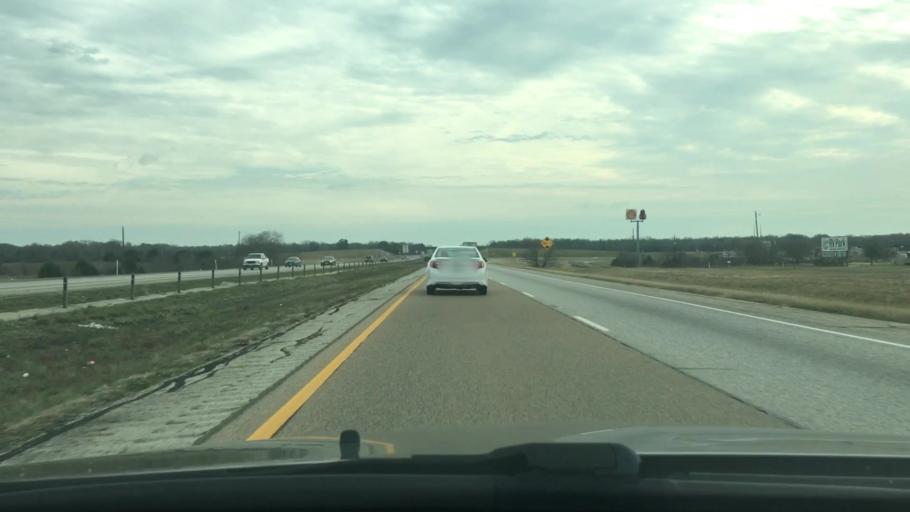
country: US
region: Texas
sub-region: Madison County
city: Madisonville
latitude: 31.0976
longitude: -95.9628
